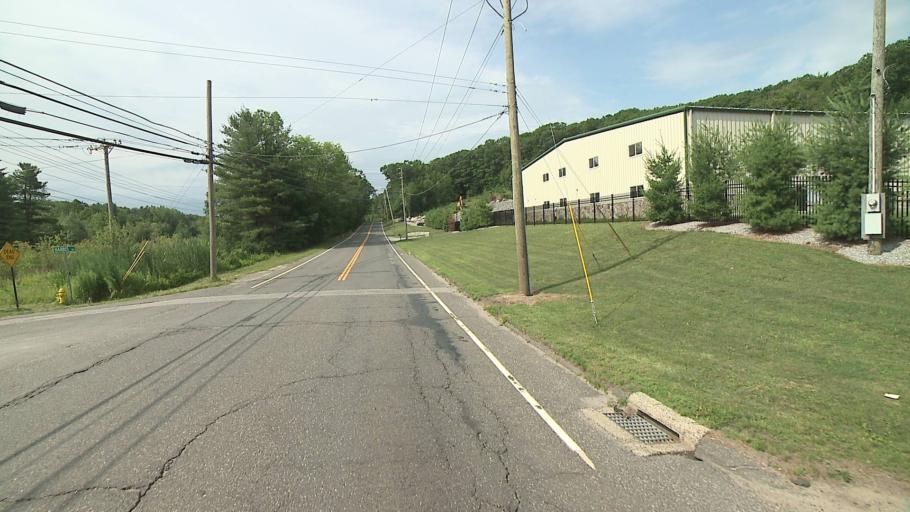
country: US
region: Connecticut
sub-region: Litchfield County
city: Torrington
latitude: 41.8535
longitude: -73.0952
